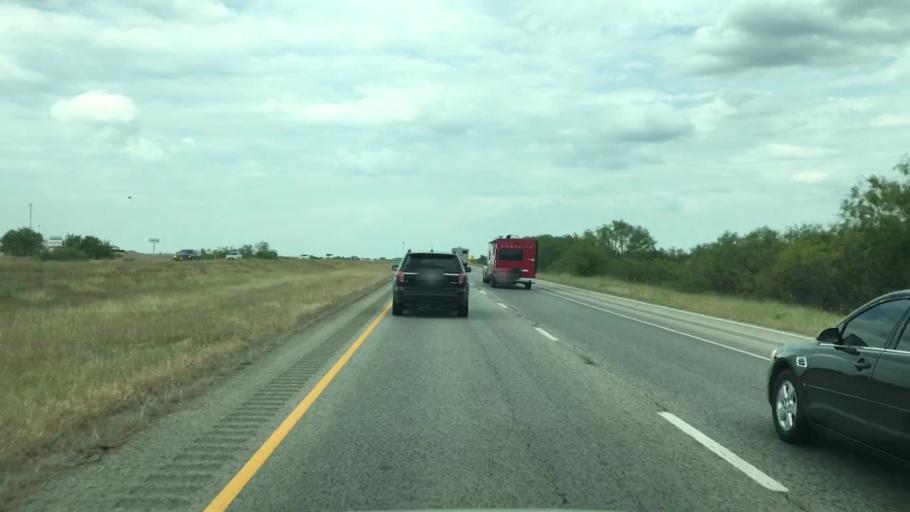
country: US
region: Texas
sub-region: Atascosa County
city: Pleasanton
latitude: 29.0990
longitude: -98.4325
